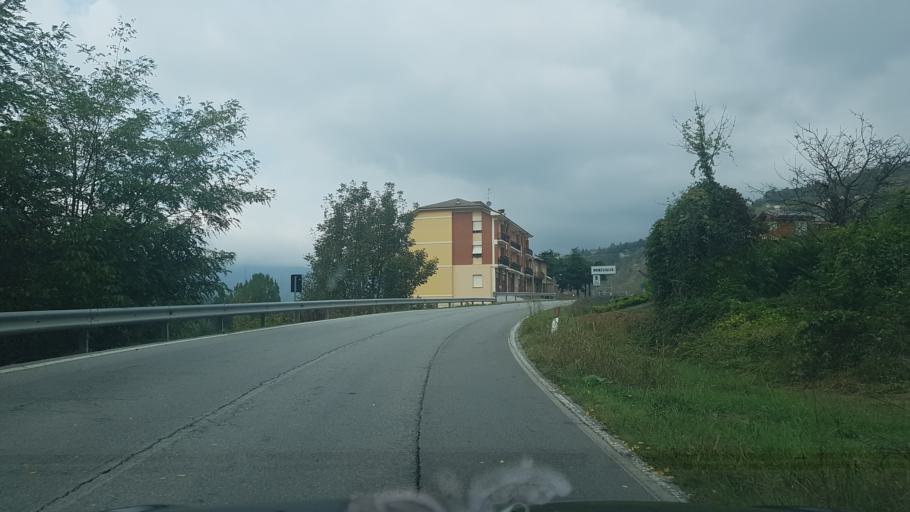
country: IT
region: Piedmont
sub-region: Provincia di Cuneo
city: Monesiglio
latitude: 44.4644
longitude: 8.1147
